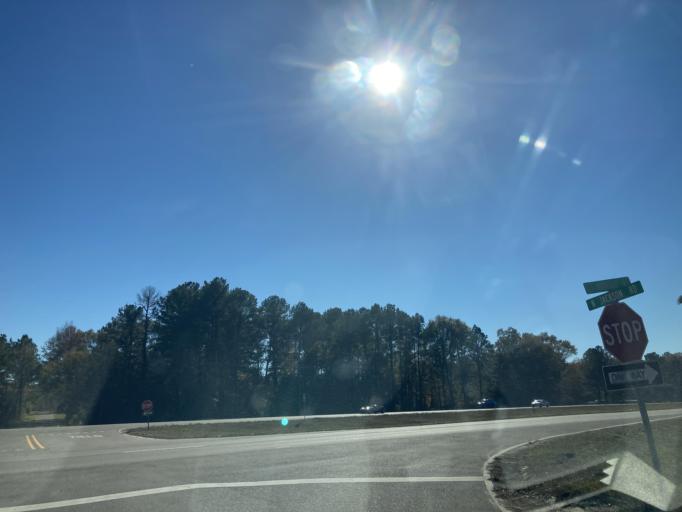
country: US
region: Mississippi
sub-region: Lamar County
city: Sumrall
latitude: 31.2861
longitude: -89.6454
